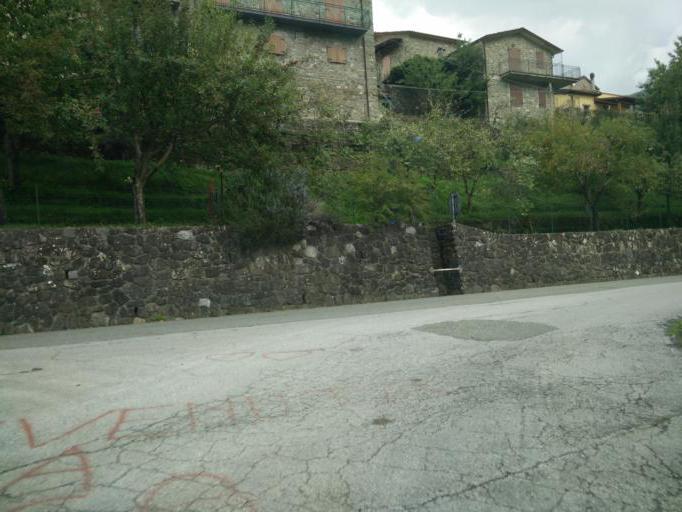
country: IT
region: Tuscany
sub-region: Provincia di Massa-Carrara
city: Casola in Lunigiana
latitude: 44.2021
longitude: 10.1767
